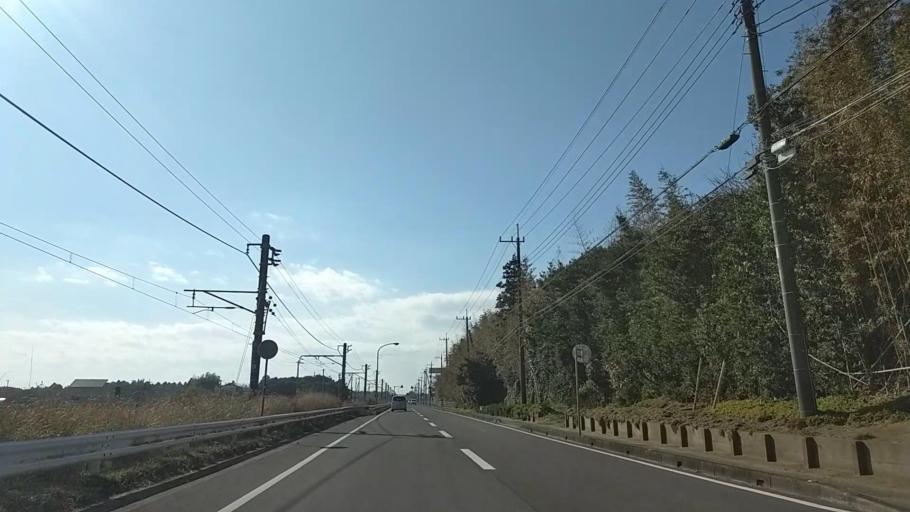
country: JP
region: Chiba
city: Yokaichiba
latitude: 35.6827
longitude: 140.5173
